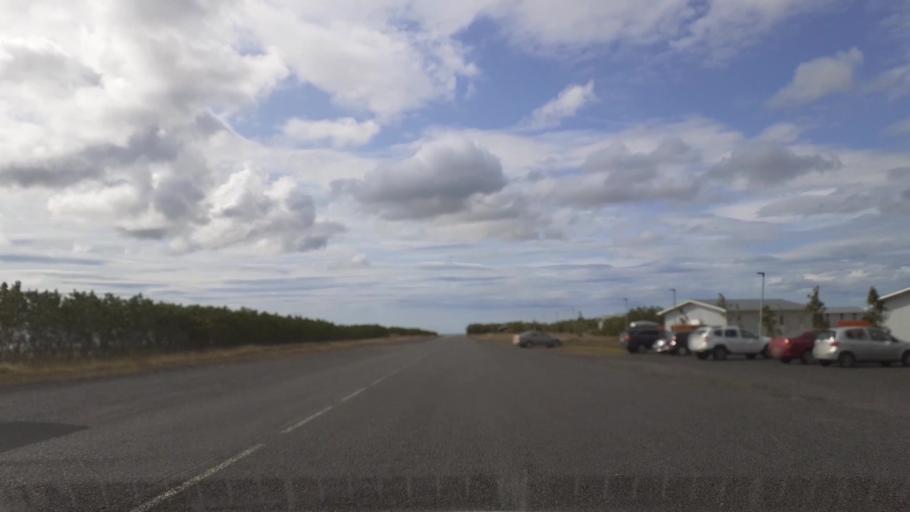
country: IS
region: South
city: Vestmannaeyjar
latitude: 63.8314
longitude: -20.3969
